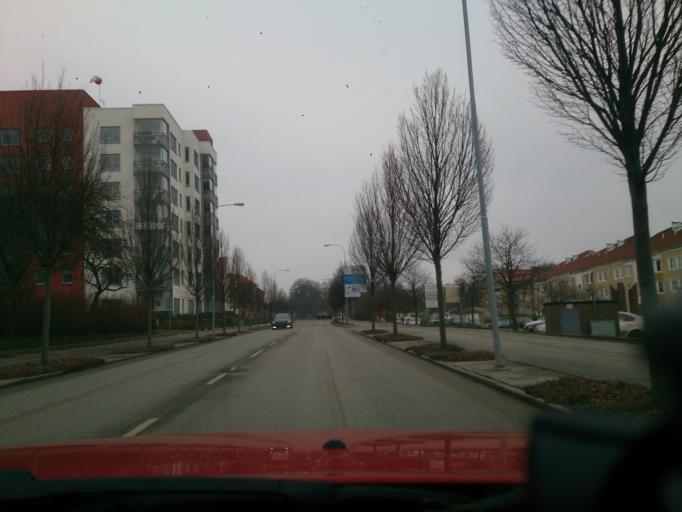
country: SE
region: Skane
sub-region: Ystads Kommun
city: Ystad
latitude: 55.4274
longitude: 13.8064
